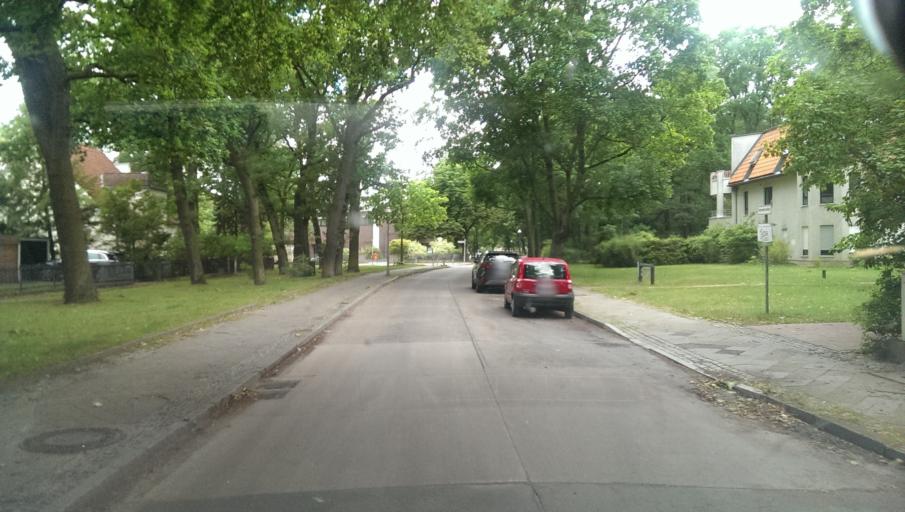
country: DE
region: Berlin
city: Zehlendorf Bezirk
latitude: 52.4216
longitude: 13.2608
